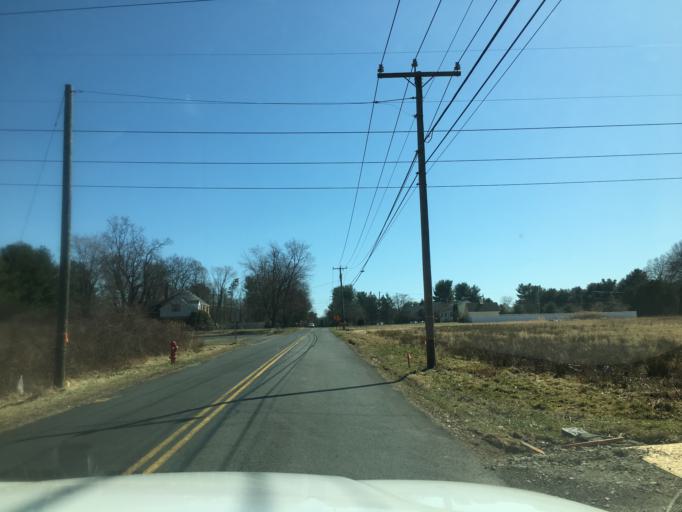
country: US
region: Connecticut
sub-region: Hartford County
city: East Hartford
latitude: 41.8086
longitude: -72.5781
